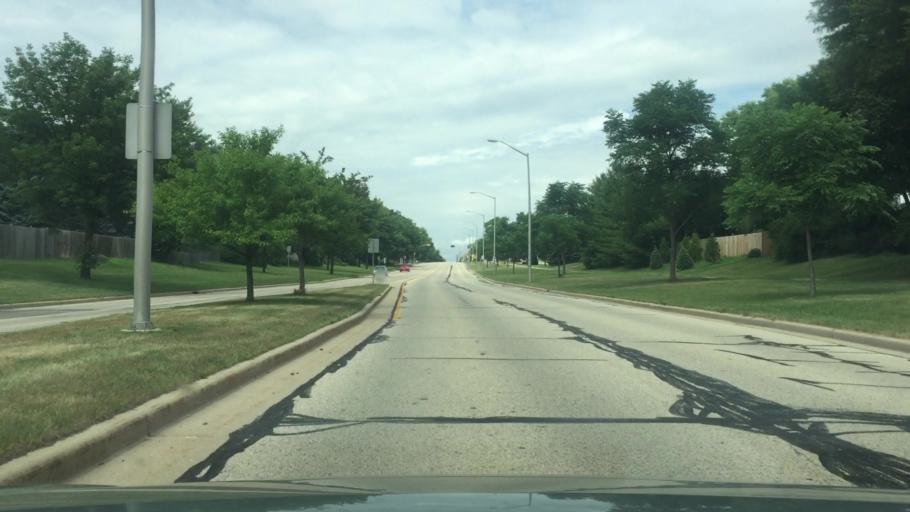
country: US
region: Wisconsin
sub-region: Waukesha County
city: Waukesha
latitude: 42.9818
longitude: -88.2273
